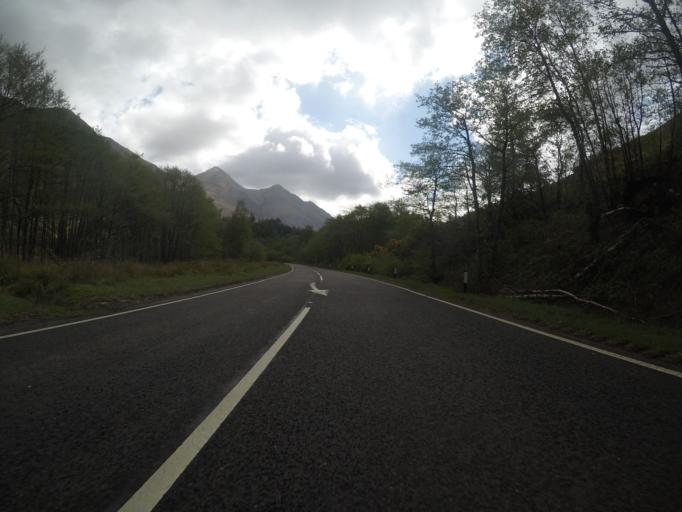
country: GB
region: Scotland
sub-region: Highland
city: Fort William
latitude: 57.2068
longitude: -5.4041
